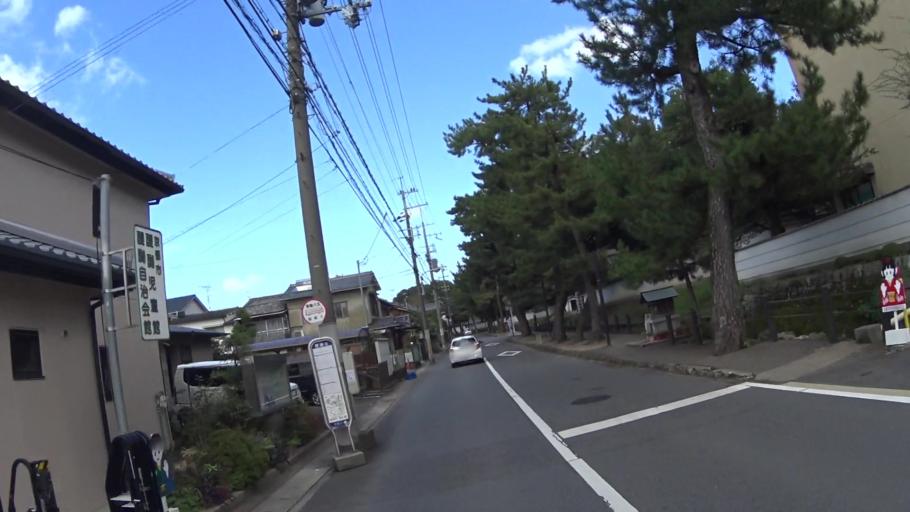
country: JP
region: Kyoto
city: Uji
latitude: 34.9501
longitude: 135.8175
